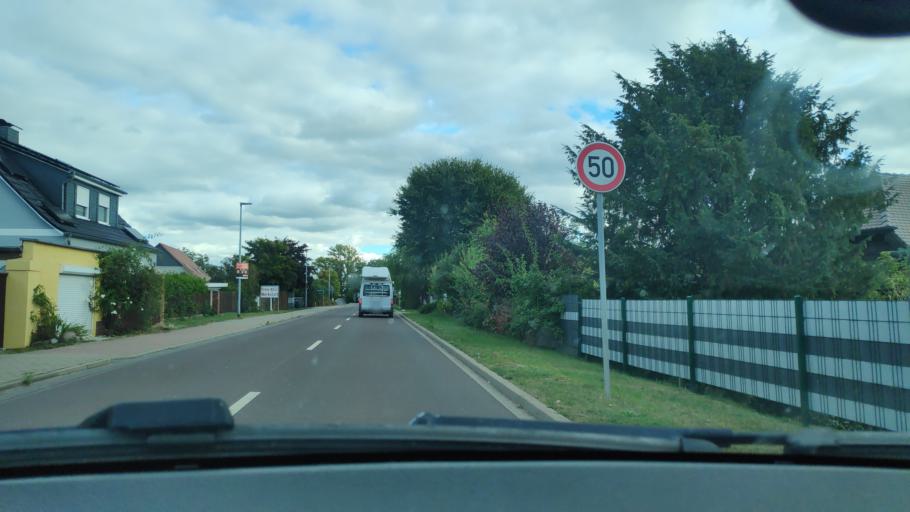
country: DE
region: Saxony-Anhalt
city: Biederitz
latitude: 52.1552
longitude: 11.7297
